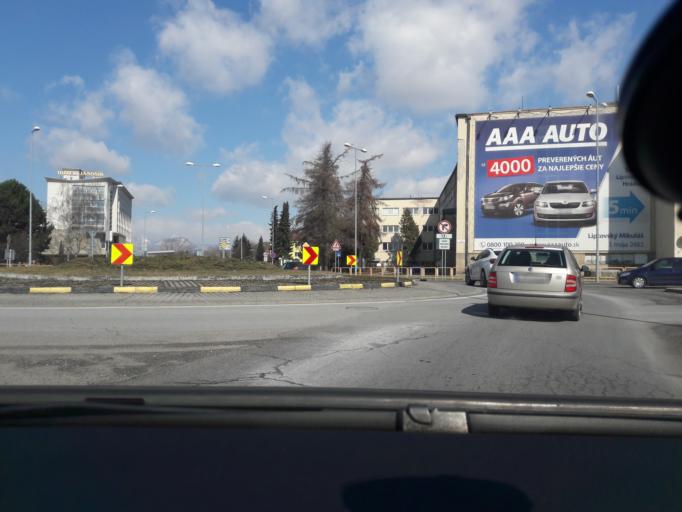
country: SK
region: Zilinsky
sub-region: Okres Liptovsky Mikulas
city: Liptovsky Mikulas
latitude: 49.0859
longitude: 19.6049
